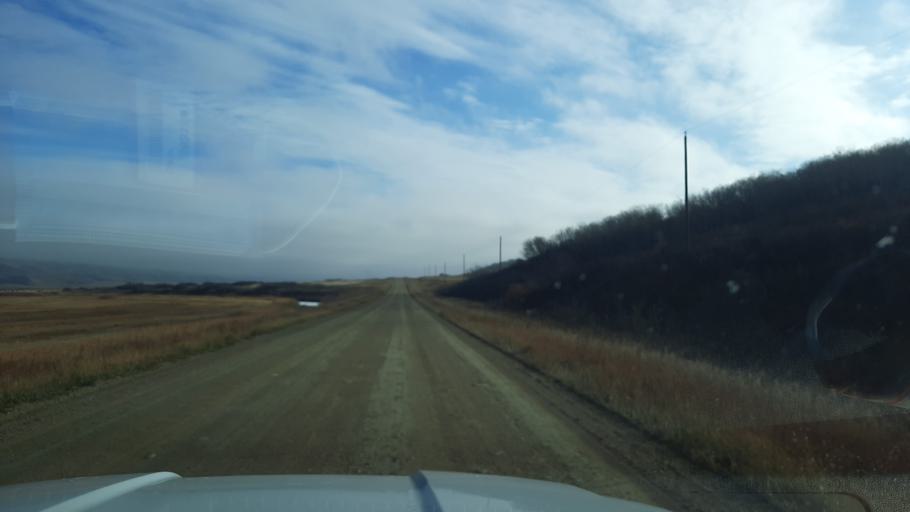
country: CA
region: Saskatchewan
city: Pilot Butte
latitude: 50.7842
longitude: -104.2181
